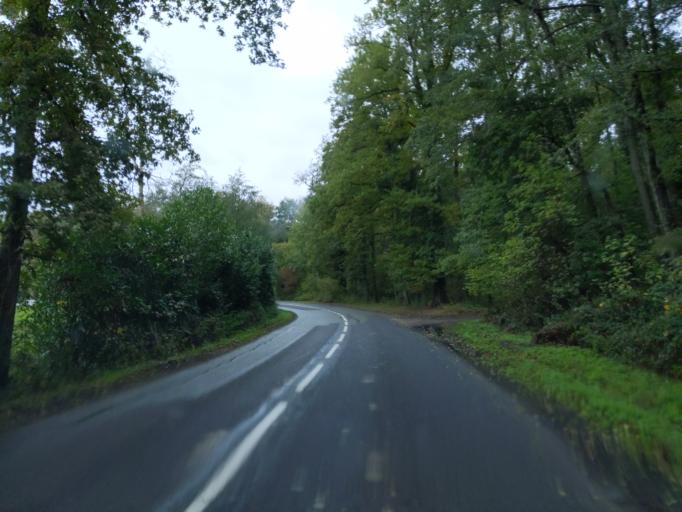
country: FR
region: Ile-de-France
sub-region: Departement des Yvelines
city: Bullion
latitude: 48.6116
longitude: 1.9624
